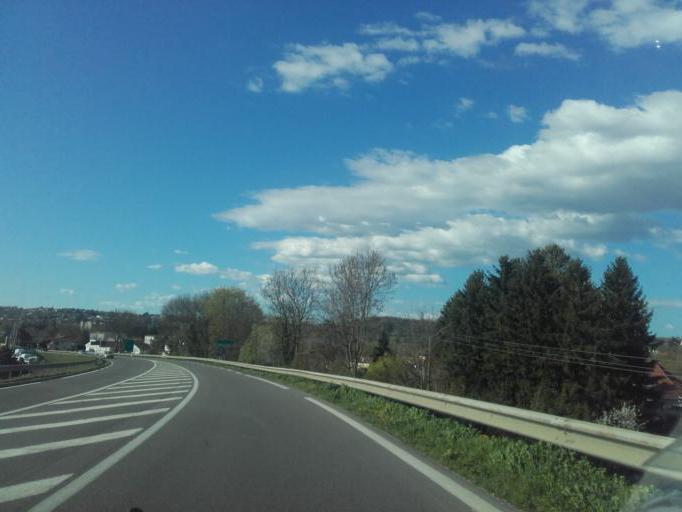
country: FR
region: Rhone-Alpes
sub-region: Departement de l'Isere
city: Bourgoin
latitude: 45.5775
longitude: 5.3020
